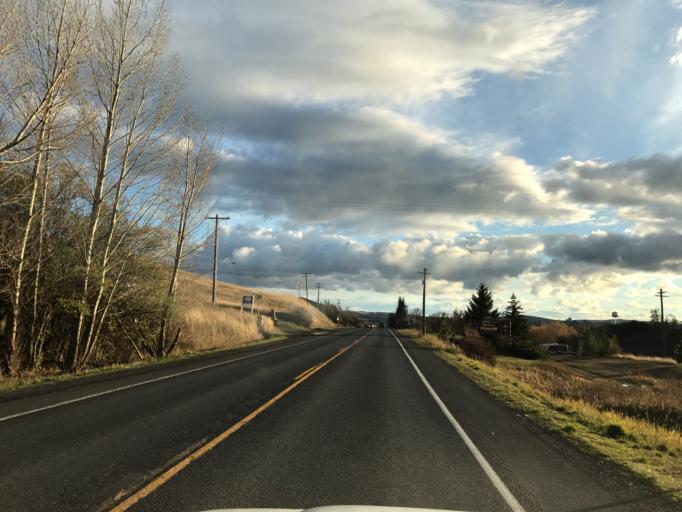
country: US
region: Idaho
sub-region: Latah County
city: Moscow
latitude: 46.7491
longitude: -117.0016
